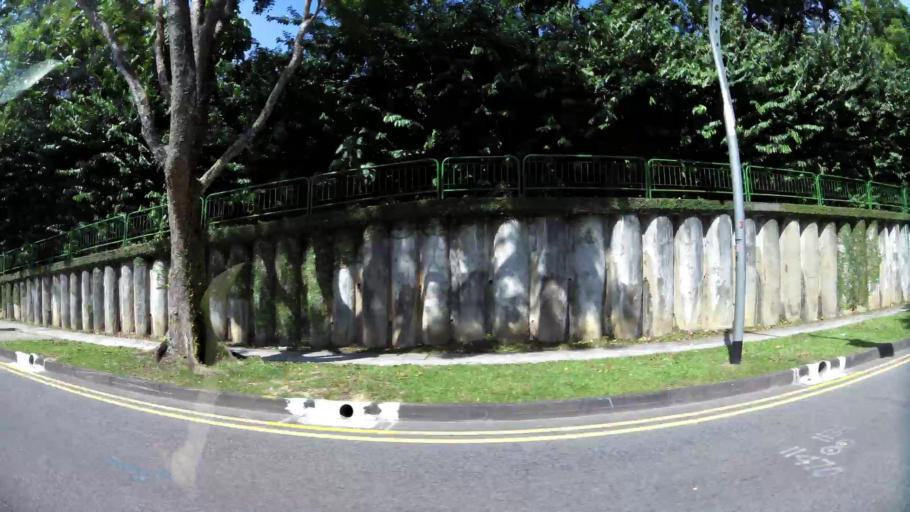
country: SG
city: Singapore
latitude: 1.3659
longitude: 103.8281
